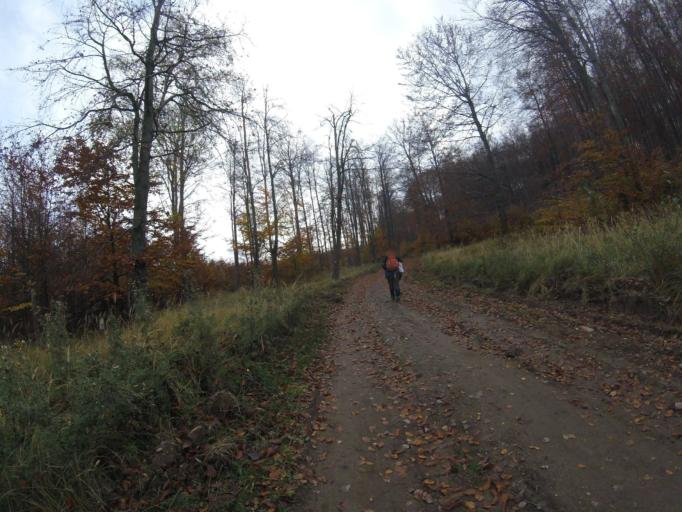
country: HU
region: Borsod-Abauj-Zemplen
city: Gonc
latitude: 48.4183
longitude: 21.3750
